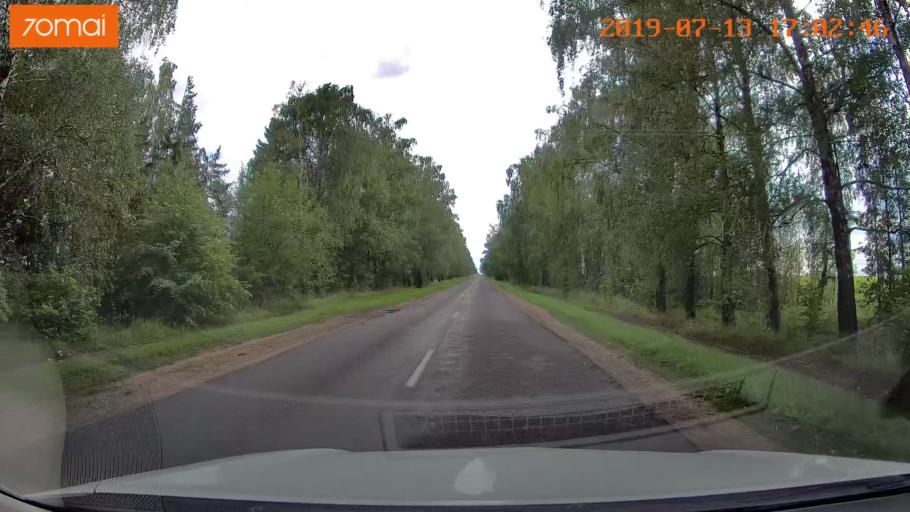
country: BY
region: Mogilev
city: Kirawsk
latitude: 53.2826
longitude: 29.3837
